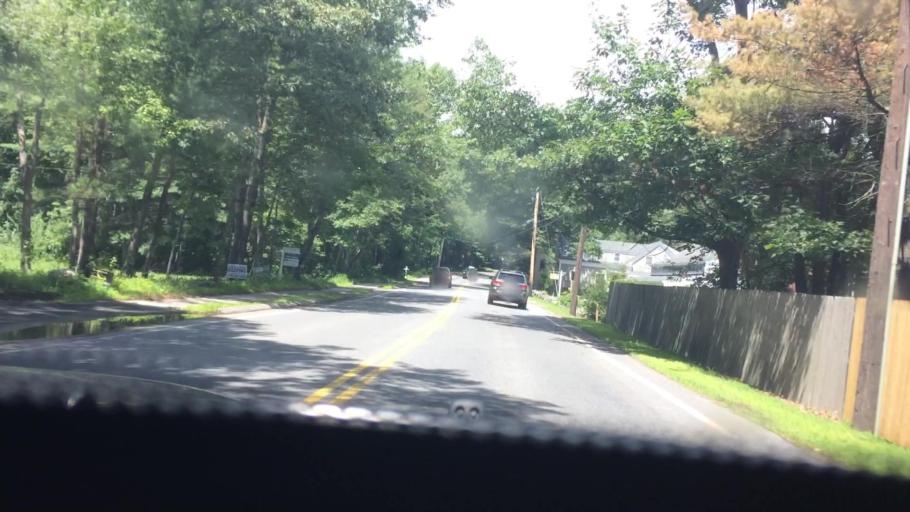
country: US
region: Massachusetts
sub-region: Middlesex County
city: Sudbury
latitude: 42.3923
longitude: -71.4230
